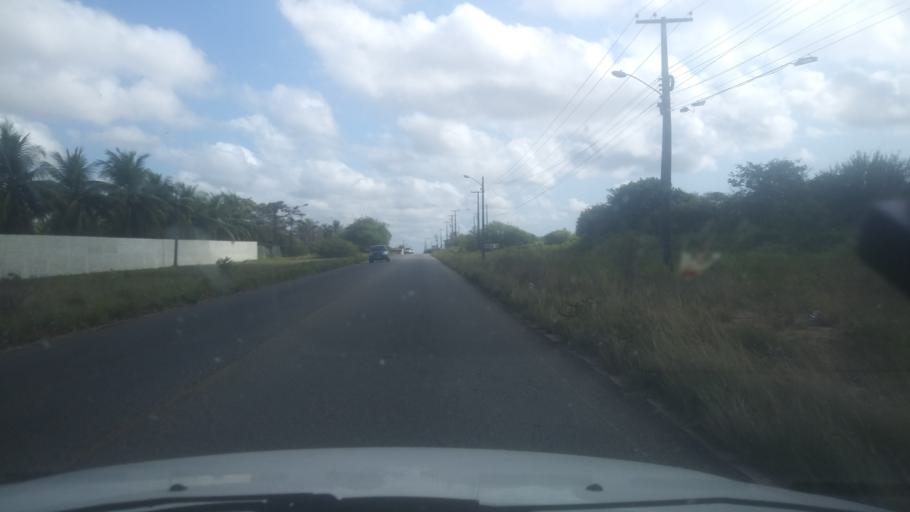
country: BR
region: Rio Grande do Norte
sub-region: Extremoz
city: Extremoz
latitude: -5.7168
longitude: -35.2774
